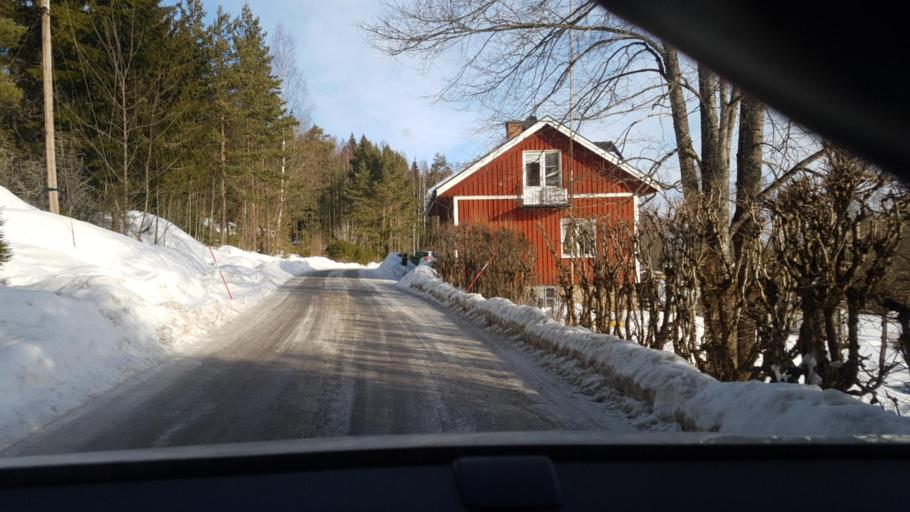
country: SE
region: Vaermland
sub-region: Eda Kommun
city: Amotfors
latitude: 59.7335
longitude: 12.2785
